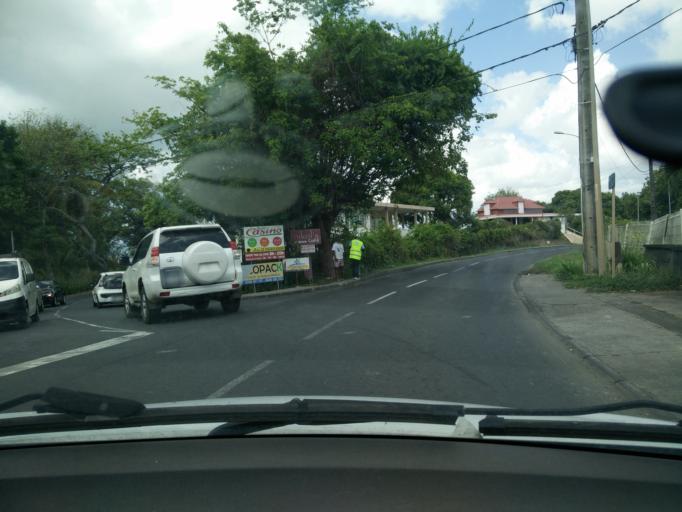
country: GP
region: Guadeloupe
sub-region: Guadeloupe
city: Les Abymes
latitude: 16.2613
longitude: -61.5046
